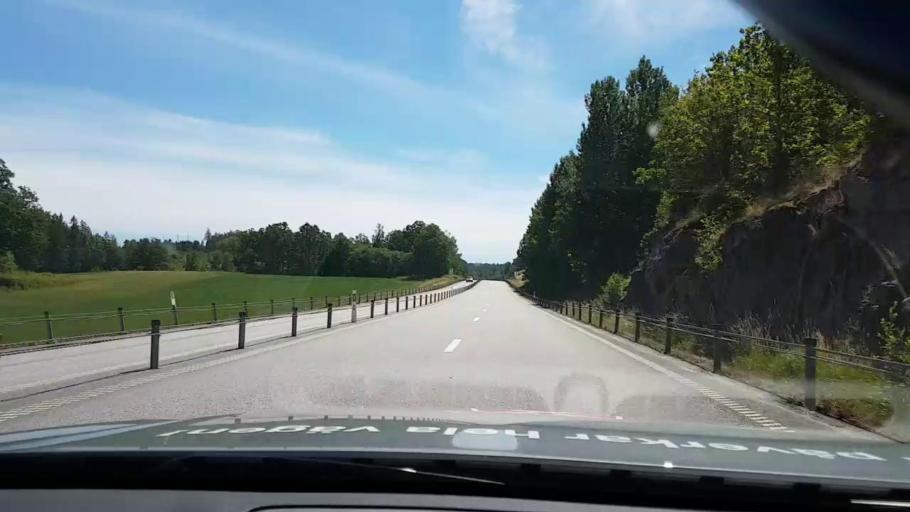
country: SE
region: Kalmar
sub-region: Vasterviks Kommun
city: Gamleby
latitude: 57.9272
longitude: 16.3975
